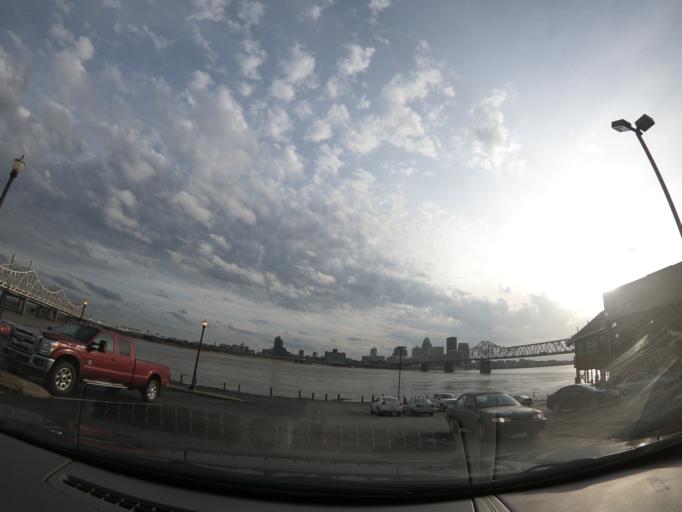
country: US
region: Indiana
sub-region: Clark County
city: Jeffersonville
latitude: 38.2680
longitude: -85.7474
